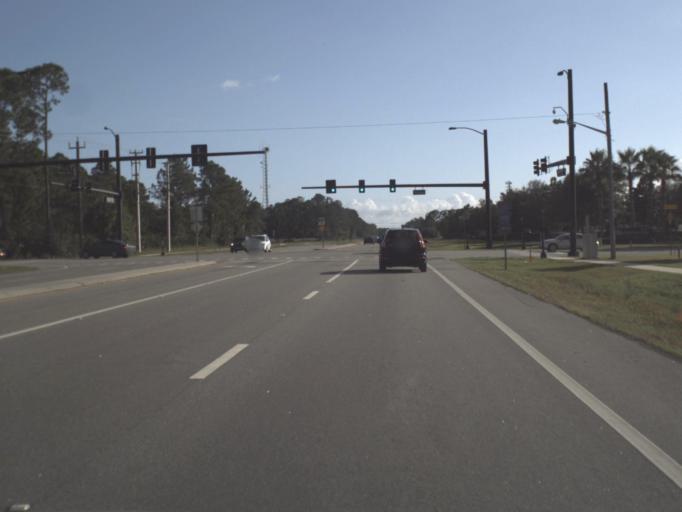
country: US
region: Florida
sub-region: Volusia County
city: Holly Hill
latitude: 29.2148
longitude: -81.0909
